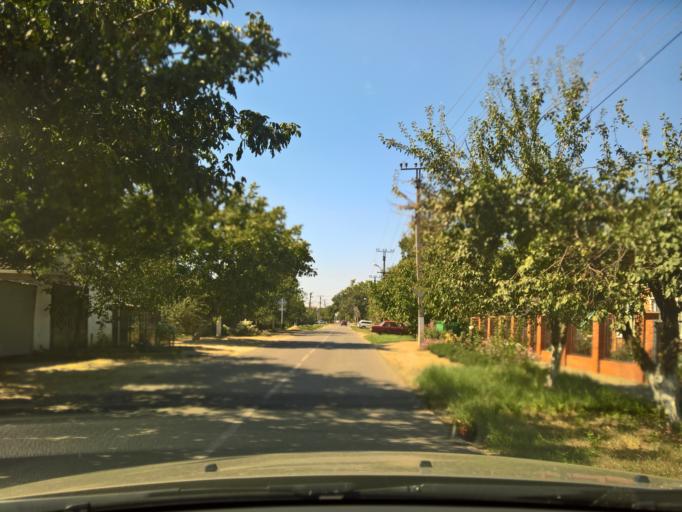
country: RU
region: Krasnodarskiy
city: Slavyansk-na-Kubani
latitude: 45.2682
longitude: 38.1234
